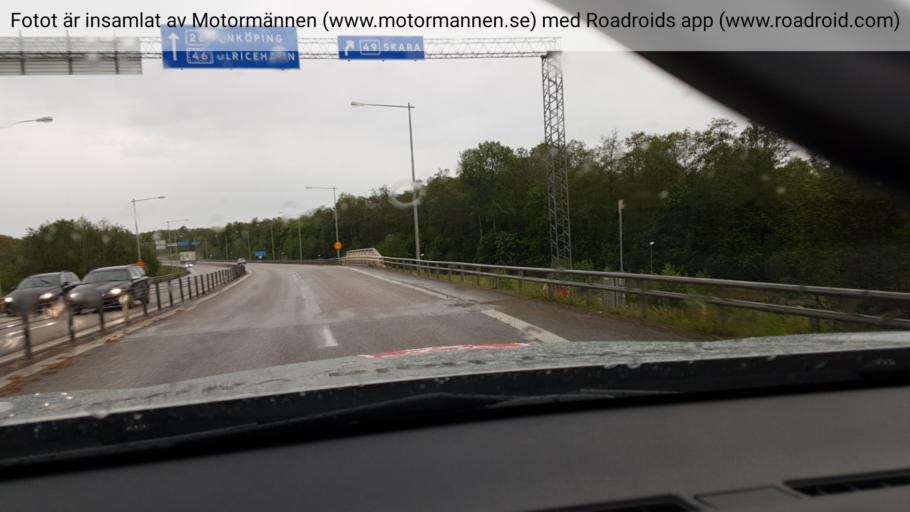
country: SE
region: Vaestra Goetaland
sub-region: Skovde Kommun
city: Skoevde
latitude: 58.3740
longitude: 13.8563
